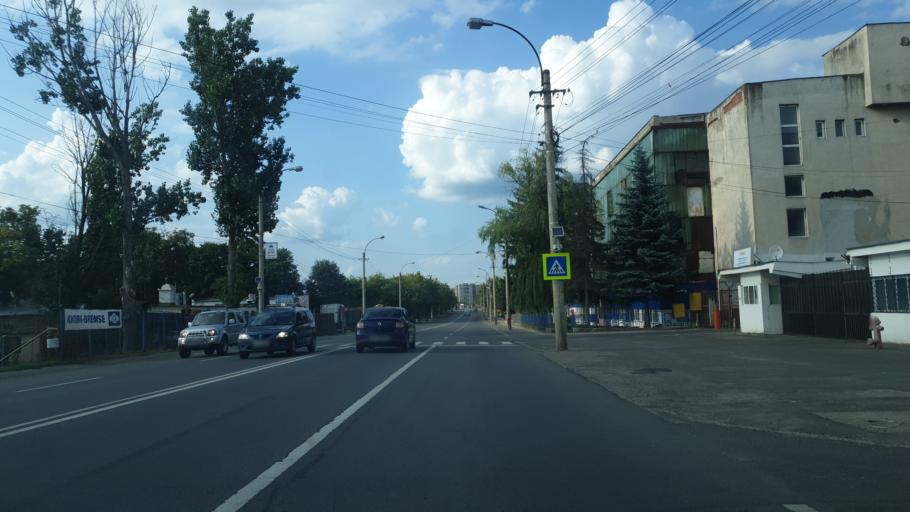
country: RO
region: Covasna
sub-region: Municipiul Sfantu Gheorghe
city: Sfantu-Gheorghe
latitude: 45.8516
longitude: 25.8060
